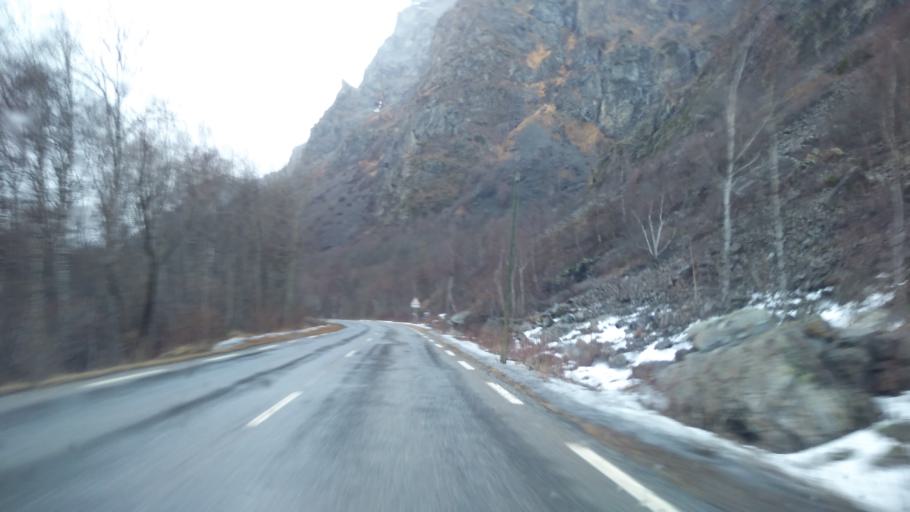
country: FR
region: Rhone-Alpes
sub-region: Departement de l'Isere
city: Mont-de-Lans
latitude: 45.0377
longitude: 6.2133
